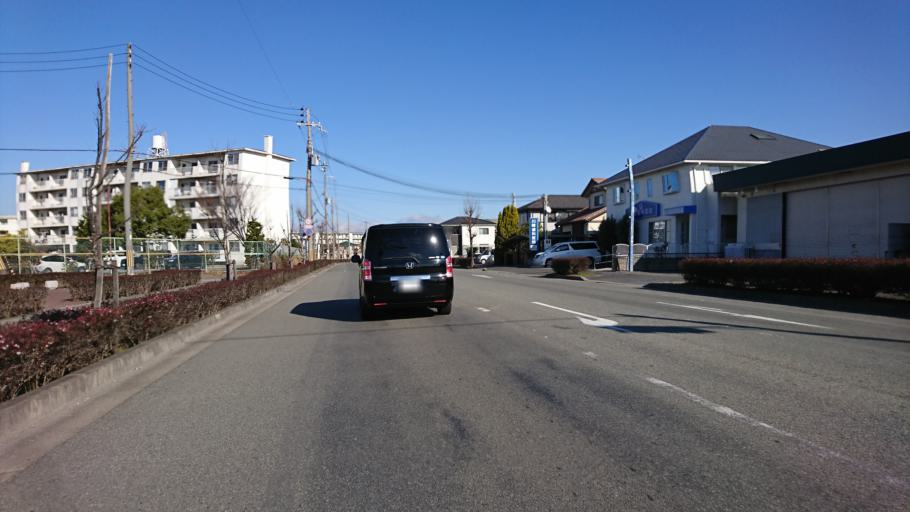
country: JP
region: Hyogo
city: Kakogawacho-honmachi
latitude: 34.7386
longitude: 134.8422
